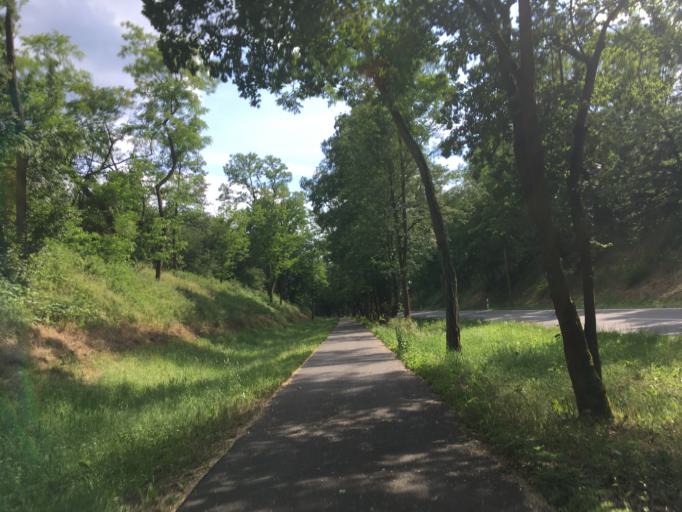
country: DE
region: Brandenburg
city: Furstenwalde
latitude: 52.3893
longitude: 14.0866
